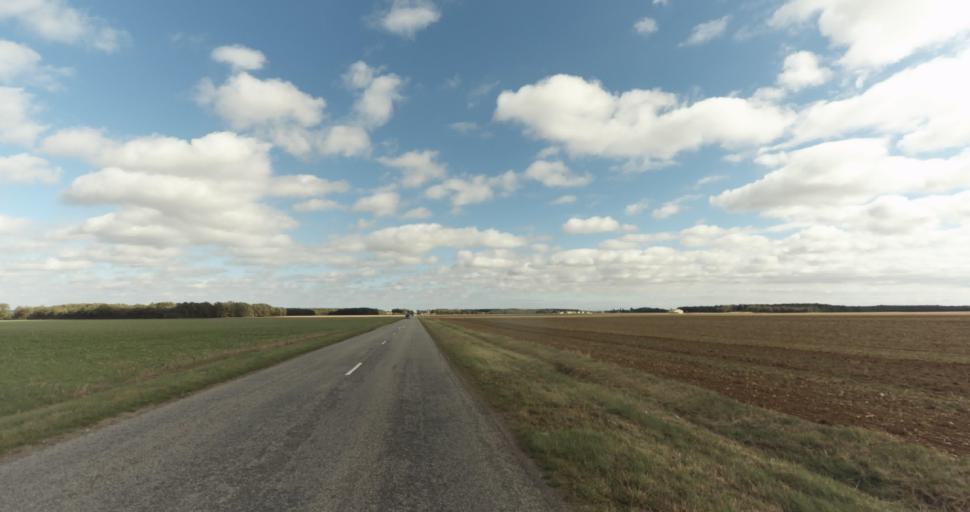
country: FR
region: Centre
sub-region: Departement d'Eure-et-Loir
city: Garnay
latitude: 48.7111
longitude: 1.3081
